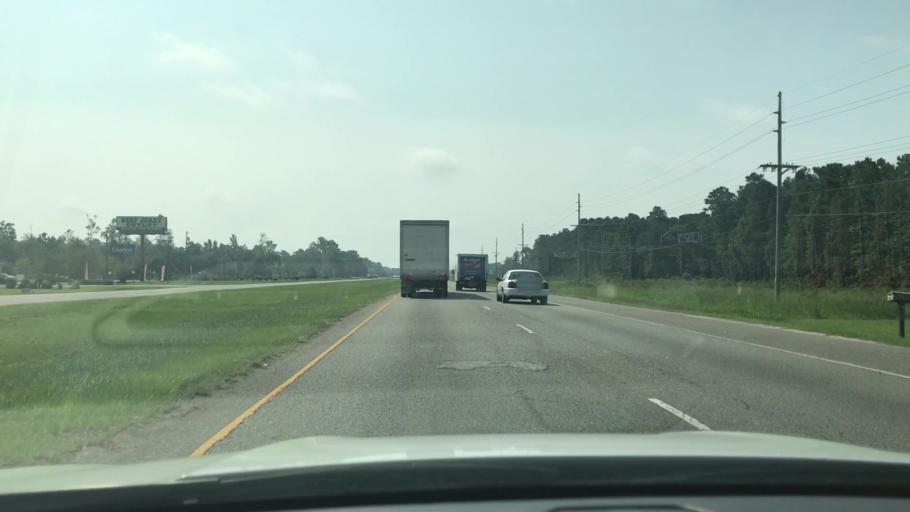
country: US
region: South Carolina
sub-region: Horry County
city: Red Hill
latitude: 33.7870
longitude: -78.9937
